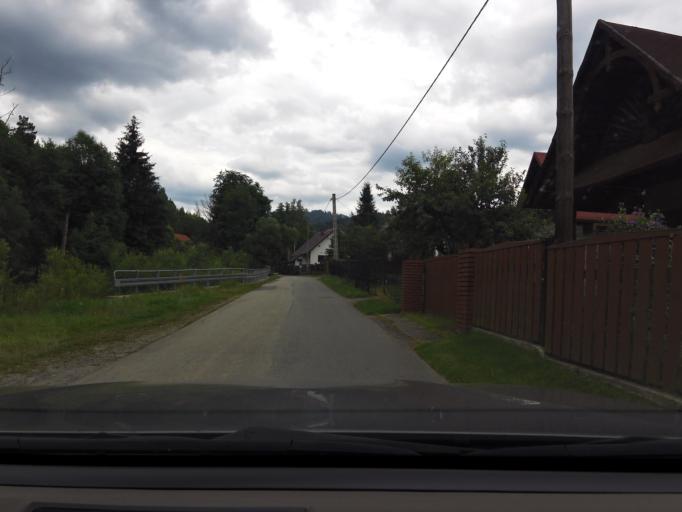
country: PL
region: Silesian Voivodeship
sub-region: Powiat zywiecki
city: Ujsoly
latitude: 49.5028
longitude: 19.1344
